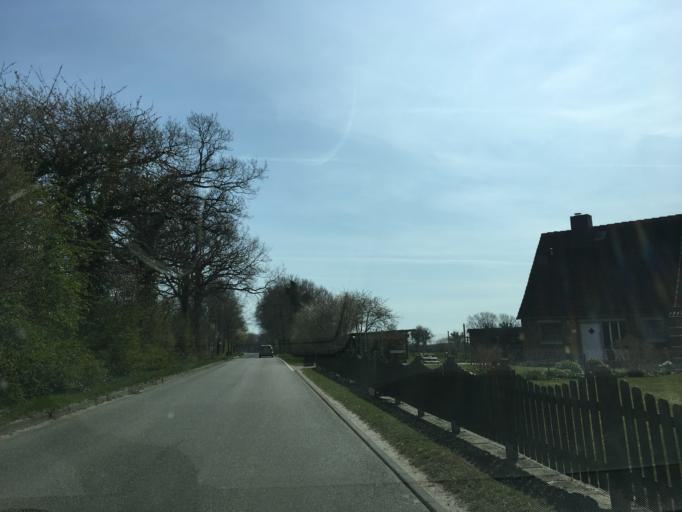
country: DE
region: Schleswig-Holstein
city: Felm
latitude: 54.3918
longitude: 10.0542
